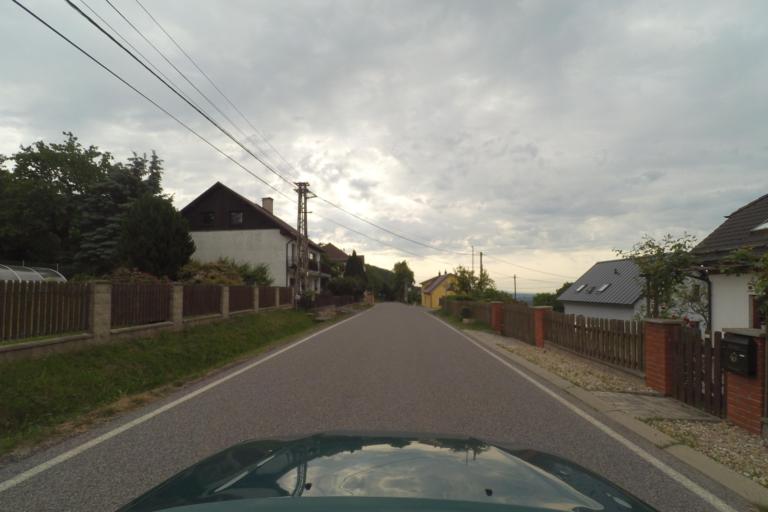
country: CZ
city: Osecna
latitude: 50.7164
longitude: 14.9742
